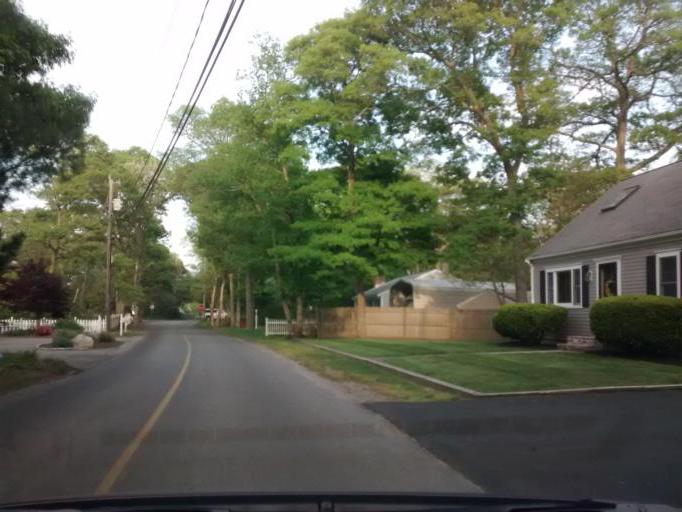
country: US
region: Massachusetts
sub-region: Barnstable County
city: East Falmouth
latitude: 41.5907
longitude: -70.5831
